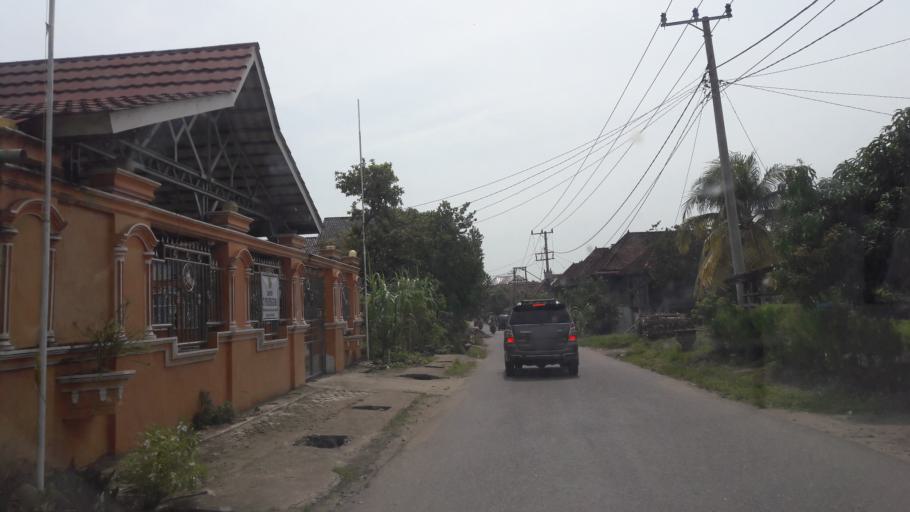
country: ID
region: South Sumatra
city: Gunungmenang
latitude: -3.1827
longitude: 104.1098
